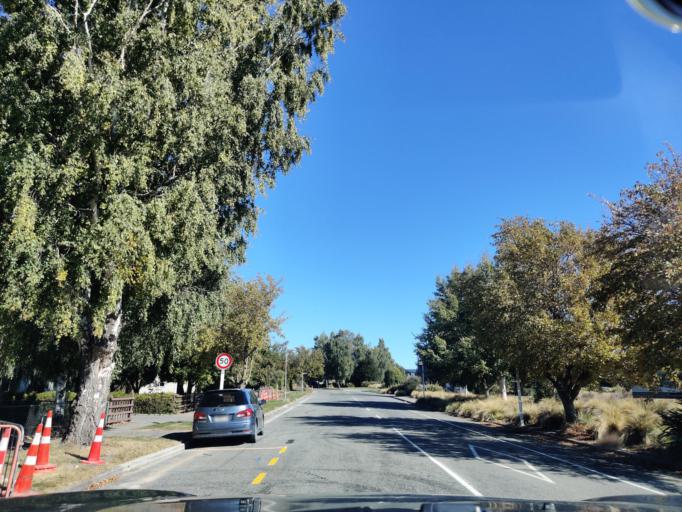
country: NZ
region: Canterbury
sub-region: Timaru District
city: Pleasant Point
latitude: -44.0056
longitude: 170.4751
